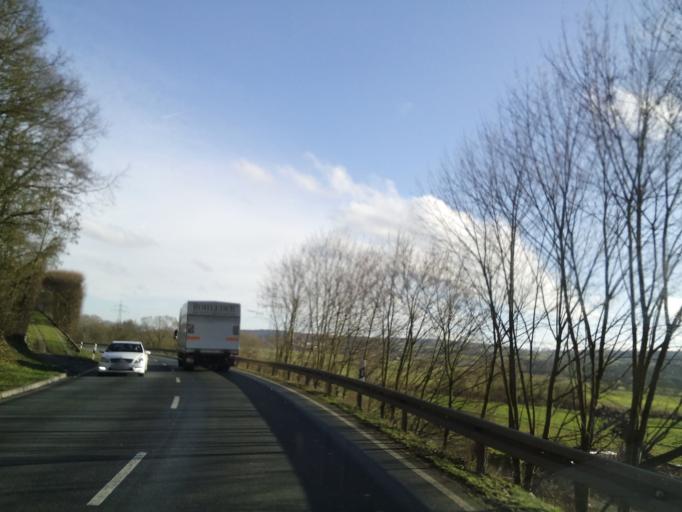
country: DE
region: Bavaria
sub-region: Upper Franconia
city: Altenkunstadt
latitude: 50.1266
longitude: 11.2816
